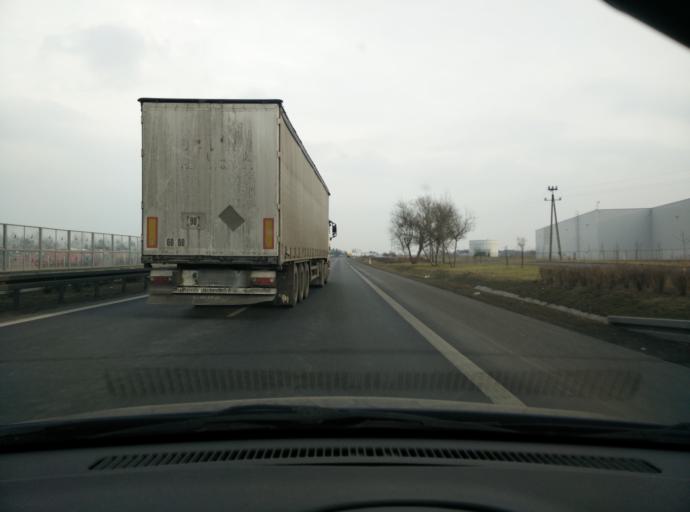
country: PL
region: Greater Poland Voivodeship
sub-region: Powiat poznanski
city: Daszewice
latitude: 52.3340
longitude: 17.0156
